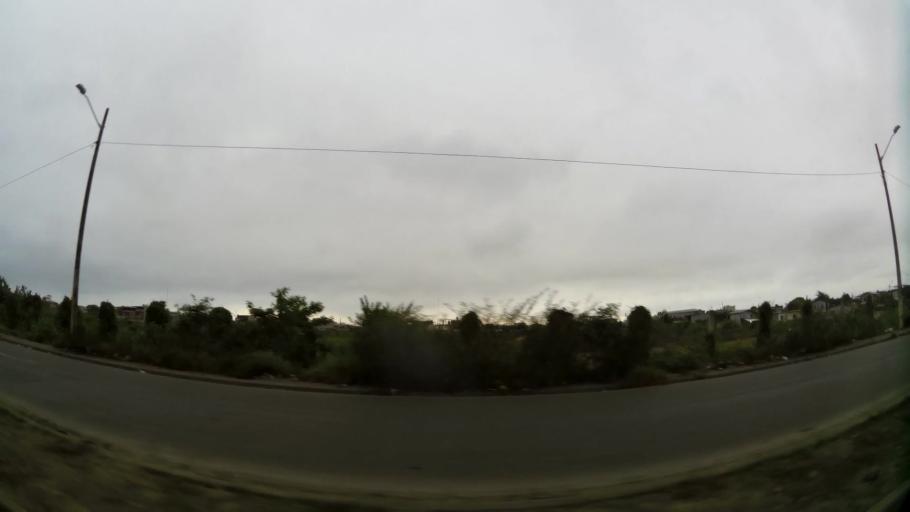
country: EC
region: El Oro
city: Machala
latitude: -3.2447
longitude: -79.9663
